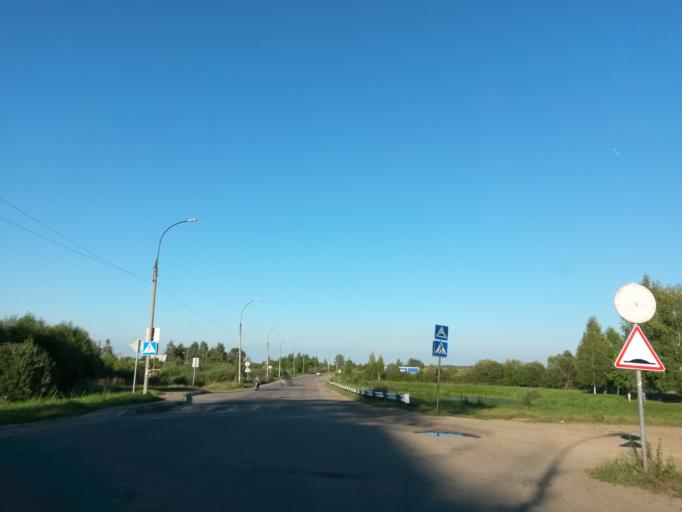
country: RU
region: Jaroslavl
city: Gavrilov-Yam
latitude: 57.3070
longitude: 39.8678
